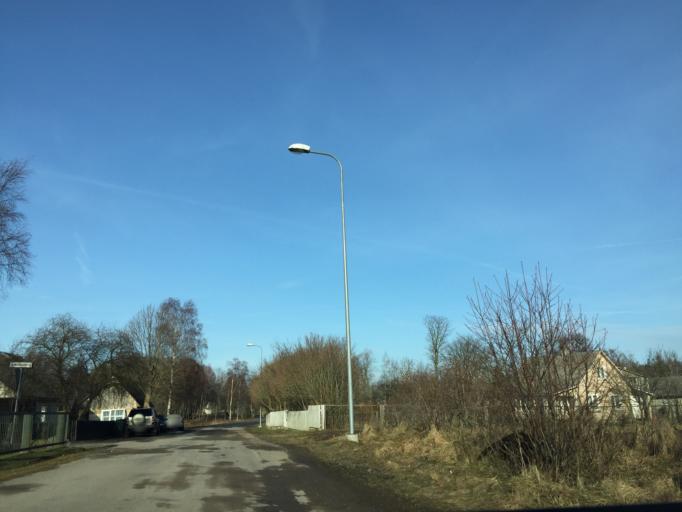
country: EE
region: Saare
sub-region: Kuressaare linn
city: Kuressaare
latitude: 58.3641
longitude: 22.0349
